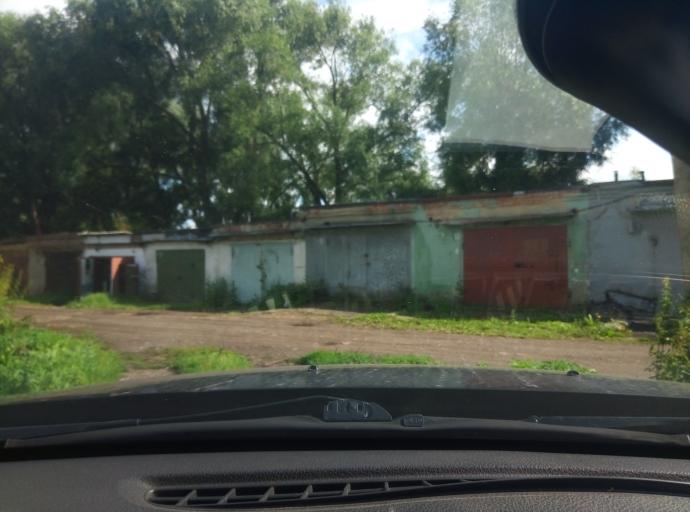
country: RU
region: Tula
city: Novomoskovsk
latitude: 53.9995
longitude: 38.2930
